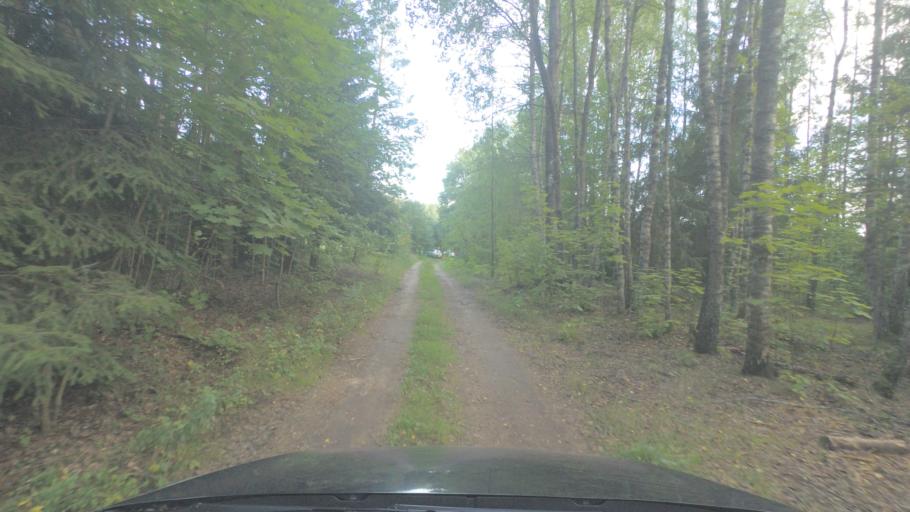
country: LT
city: Svencioneliai
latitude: 55.1600
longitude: 25.8531
